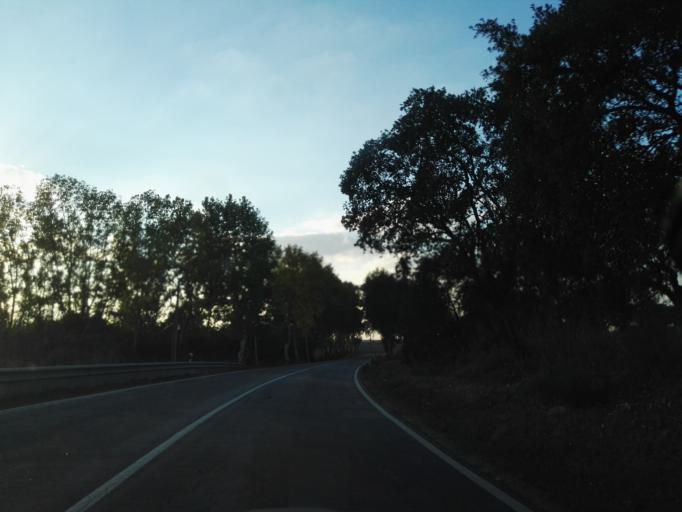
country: PT
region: Evora
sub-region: Mora
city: Mora
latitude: 38.8940
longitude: -8.0351
